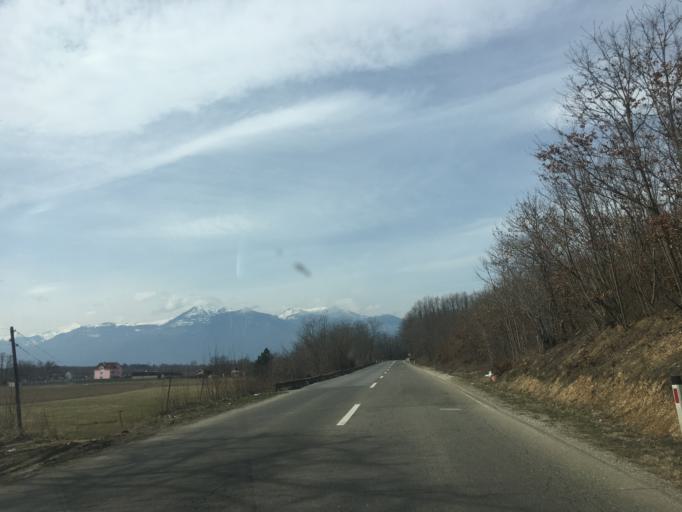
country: XK
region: Pec
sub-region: Komuna e Pejes
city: Kosuriq
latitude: 42.6383
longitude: 20.4340
